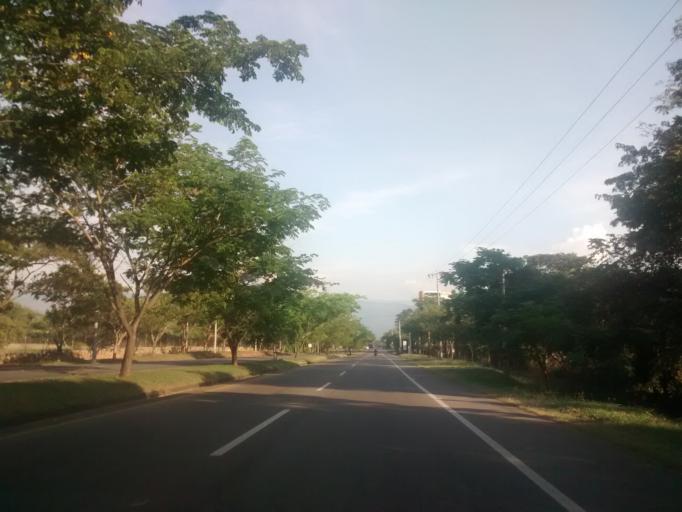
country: CO
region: Tolima
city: Melgar
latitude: 4.2266
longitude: -74.6997
